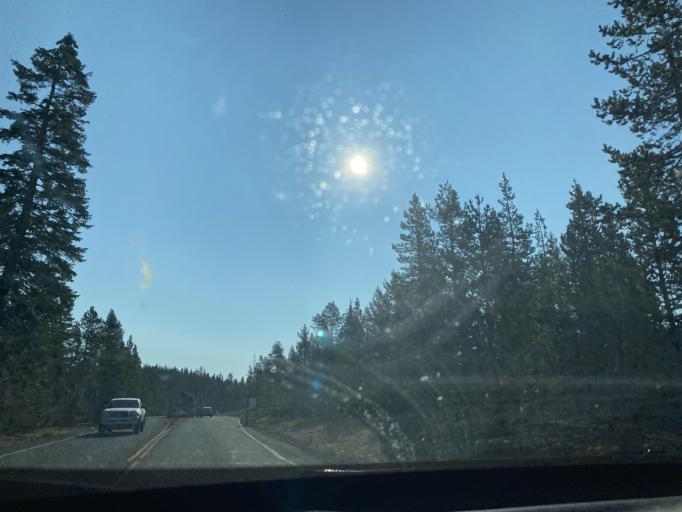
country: US
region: Oregon
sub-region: Deschutes County
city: Three Rivers
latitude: 43.7056
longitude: -121.3011
